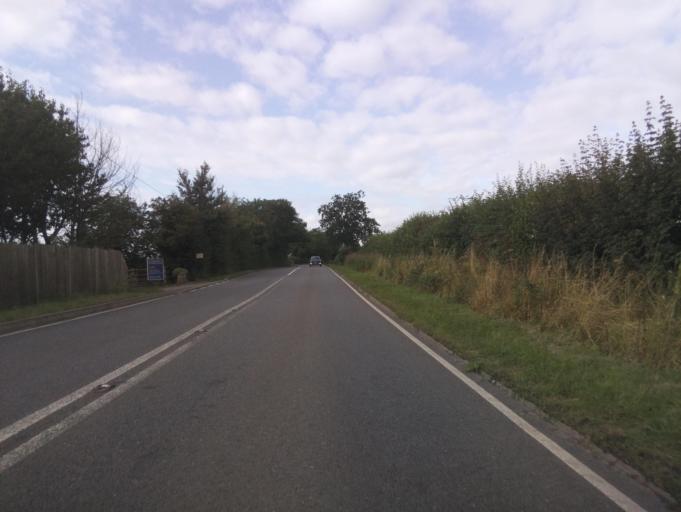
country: GB
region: England
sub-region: Warwickshire
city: Dunchurch
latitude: 52.3254
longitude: -1.3021
